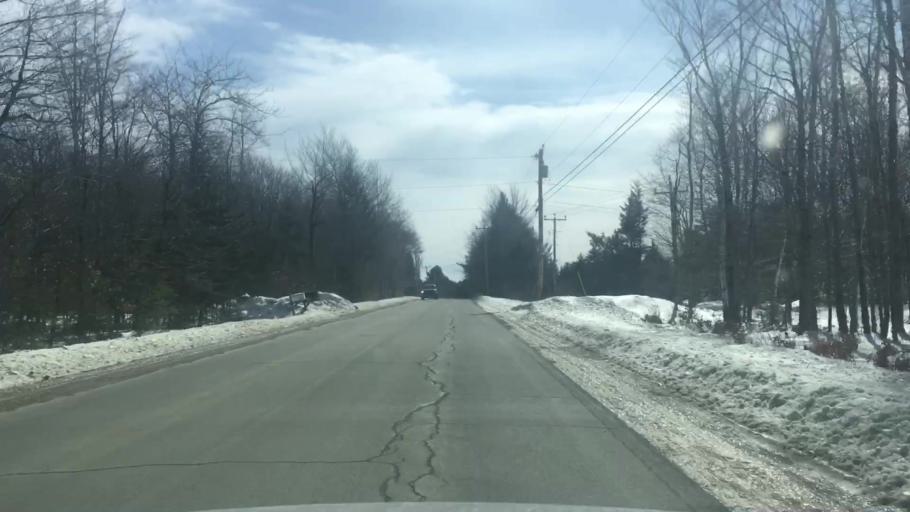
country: US
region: Maine
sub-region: Penobscot County
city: Holden
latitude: 44.7707
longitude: -68.6488
